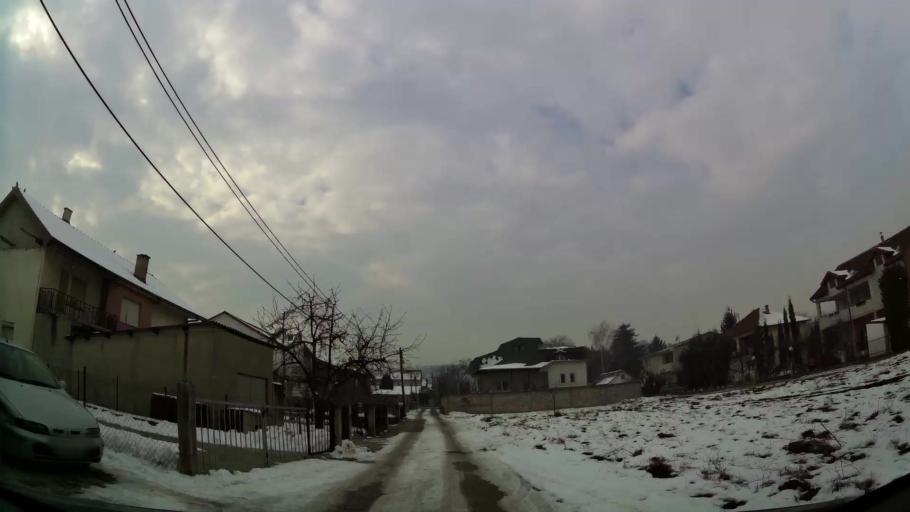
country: MK
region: Saraj
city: Saraj
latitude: 42.0230
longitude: 21.3509
